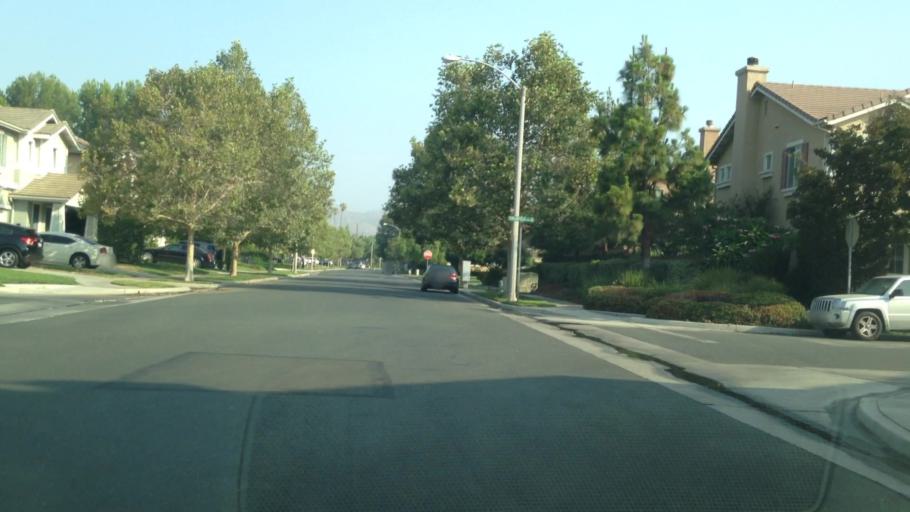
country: US
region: California
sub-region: Riverside County
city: Home Gardens
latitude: 33.9145
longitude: -117.4903
